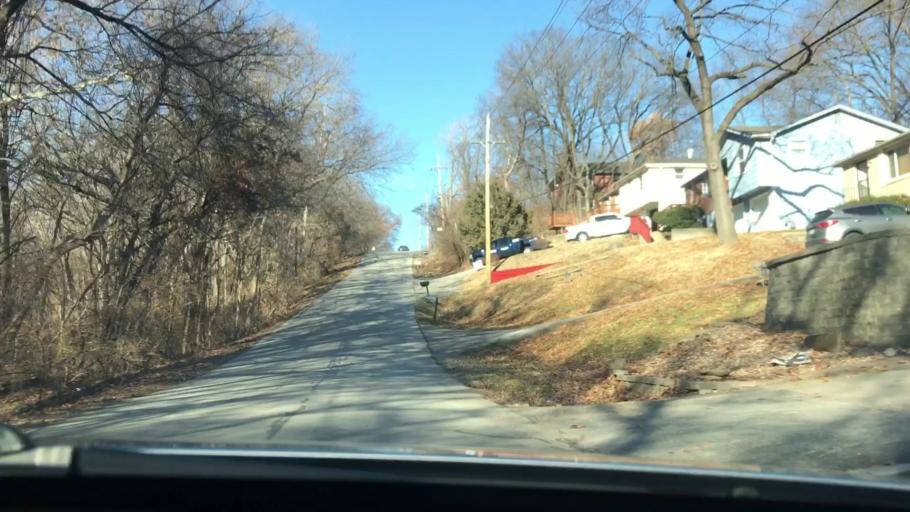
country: US
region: Missouri
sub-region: Platte County
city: Parkville
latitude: 39.1992
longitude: -94.6872
